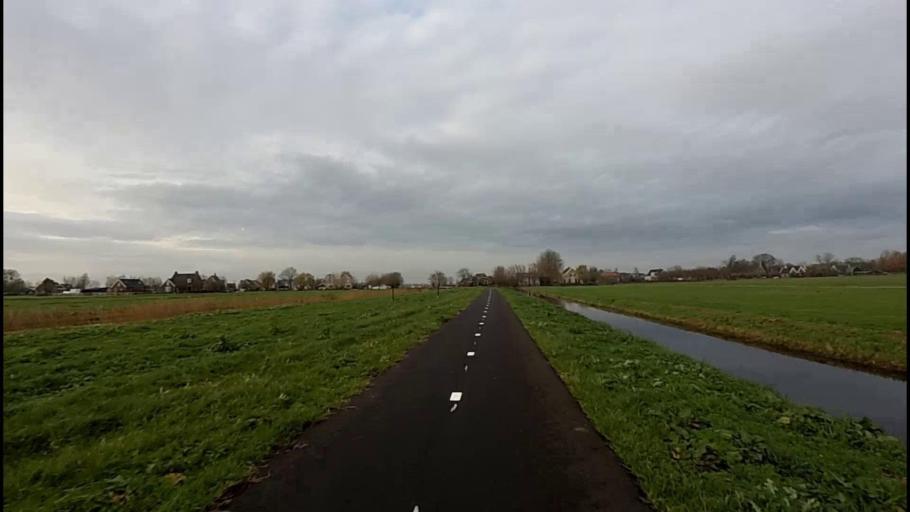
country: NL
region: South Holland
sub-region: Gemeente Vlist
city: Haastrecht
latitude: 51.9597
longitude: 4.7428
